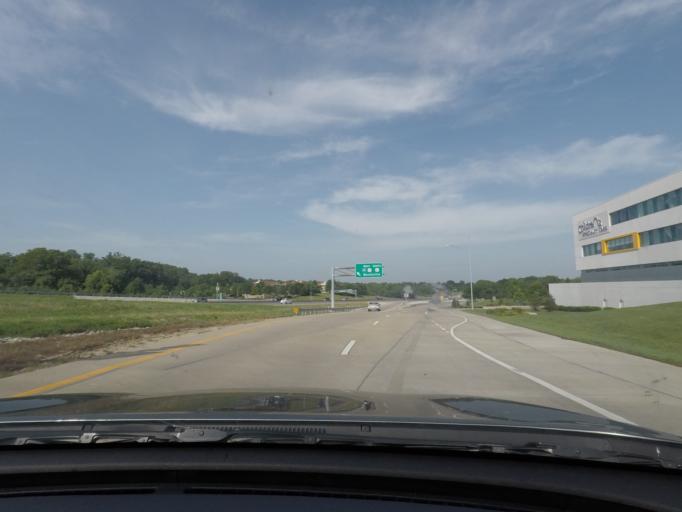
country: US
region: Missouri
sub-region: Saint Louis County
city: Town and Country
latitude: 38.6392
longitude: -90.4829
